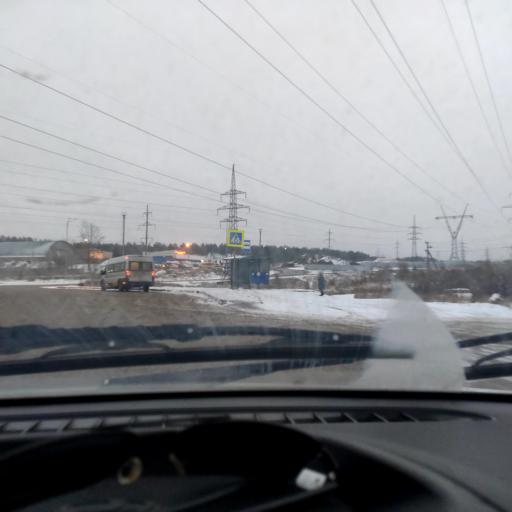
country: RU
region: Samara
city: Zhigulevsk
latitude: 53.4897
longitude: 49.5293
